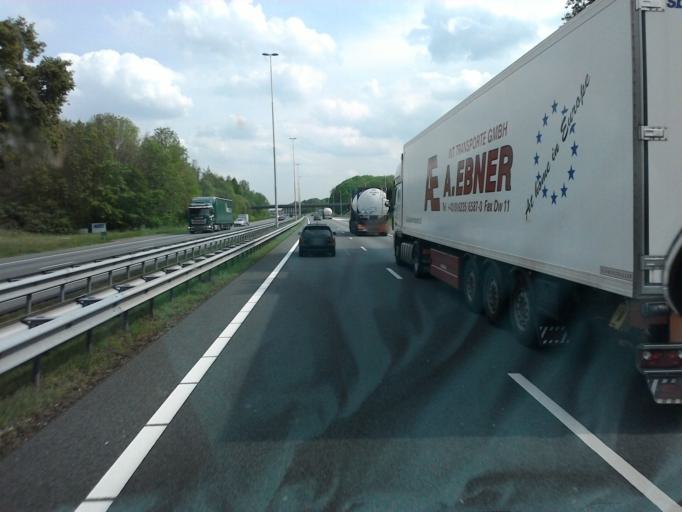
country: NL
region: Gelderland
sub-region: Gemeente Nijmegen
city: Lindenholt
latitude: 51.8006
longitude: 5.7927
